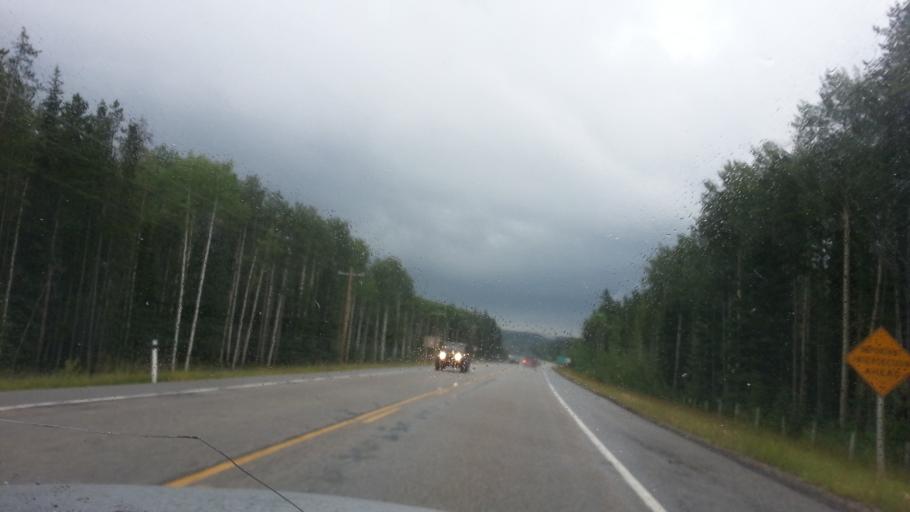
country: CA
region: Alberta
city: Cochrane
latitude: 50.9218
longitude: -114.5677
